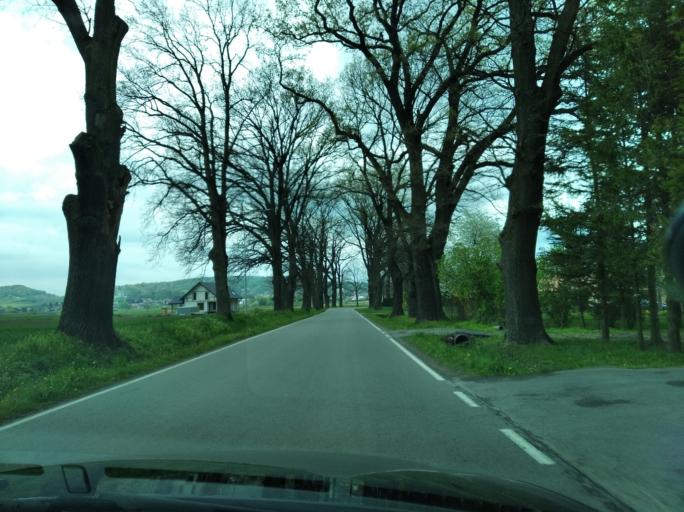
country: PL
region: Subcarpathian Voivodeship
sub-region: Powiat brzozowski
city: Turze Pole
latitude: 49.6466
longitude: 21.9960
